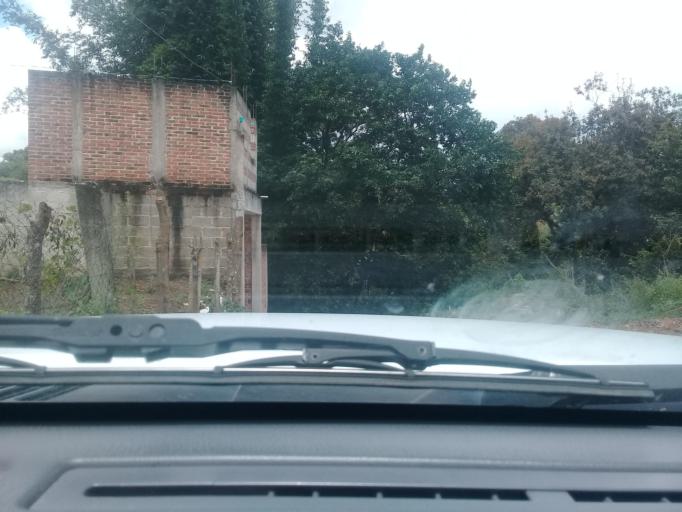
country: MX
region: Veracruz
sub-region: Tlalnelhuayocan
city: Otilpan
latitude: 19.5431
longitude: -96.9716
